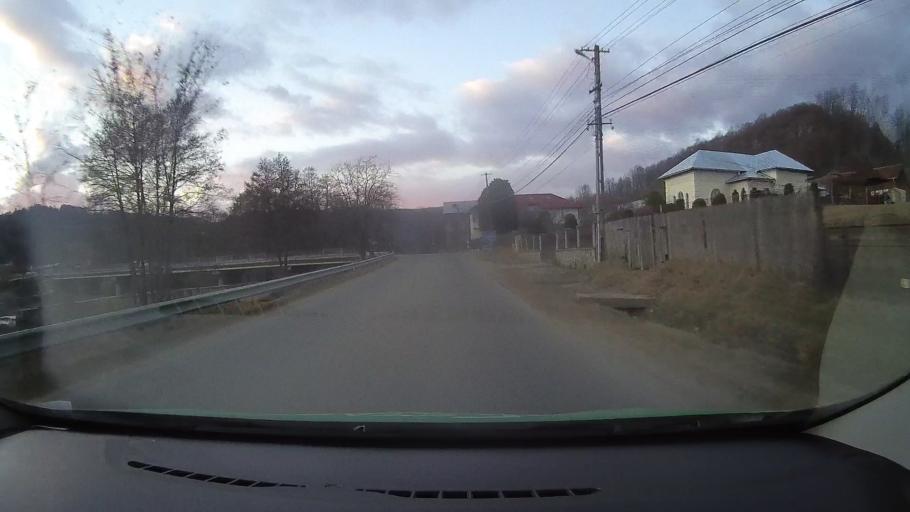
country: RO
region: Dambovita
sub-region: Comuna Valea Lunga
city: Valea Lunga-Cricov
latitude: 45.0694
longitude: 25.5808
